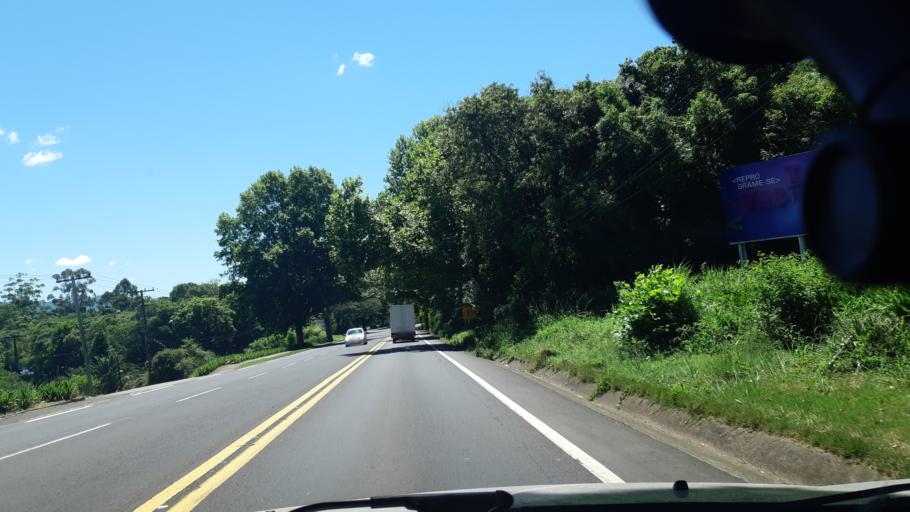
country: BR
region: Rio Grande do Sul
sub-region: Ivoti
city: Ivoti
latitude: -29.6207
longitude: -51.1256
